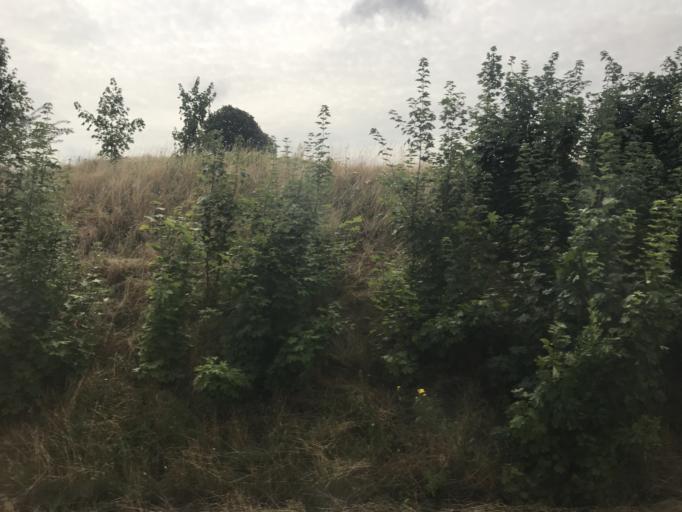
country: PL
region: Kujawsko-Pomorskie
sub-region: Powiat inowroclawski
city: Janikowo
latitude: 52.7200
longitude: 18.0491
